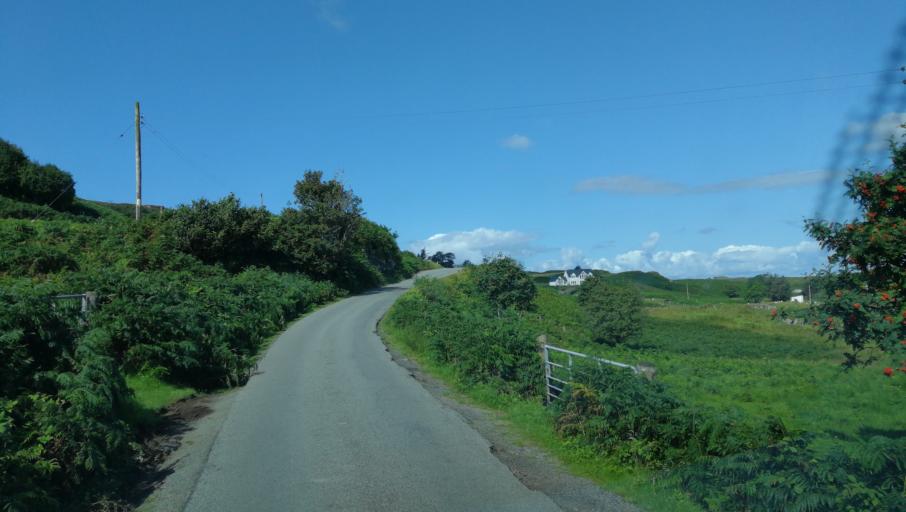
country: GB
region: Scotland
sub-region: Highland
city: Isle of Skye
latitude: 57.4482
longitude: -6.6491
